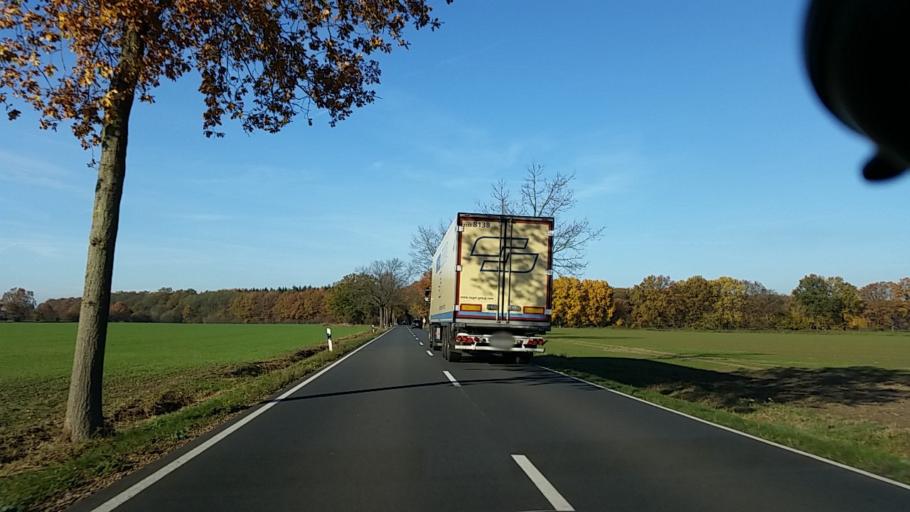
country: DE
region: Saxony-Anhalt
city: Jubar
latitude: 52.6761
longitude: 10.8416
